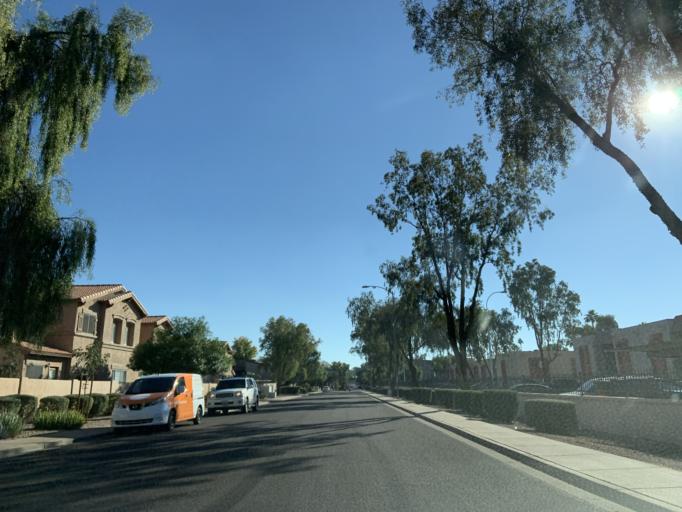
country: US
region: Arizona
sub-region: Maricopa County
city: Tempe
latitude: 33.4001
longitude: -111.8698
